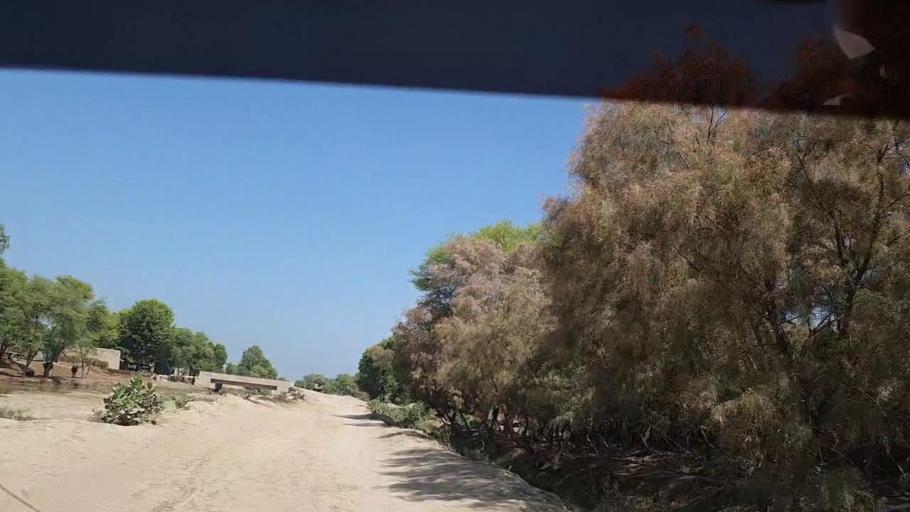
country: PK
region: Sindh
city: Tangwani
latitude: 28.2902
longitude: 69.0669
